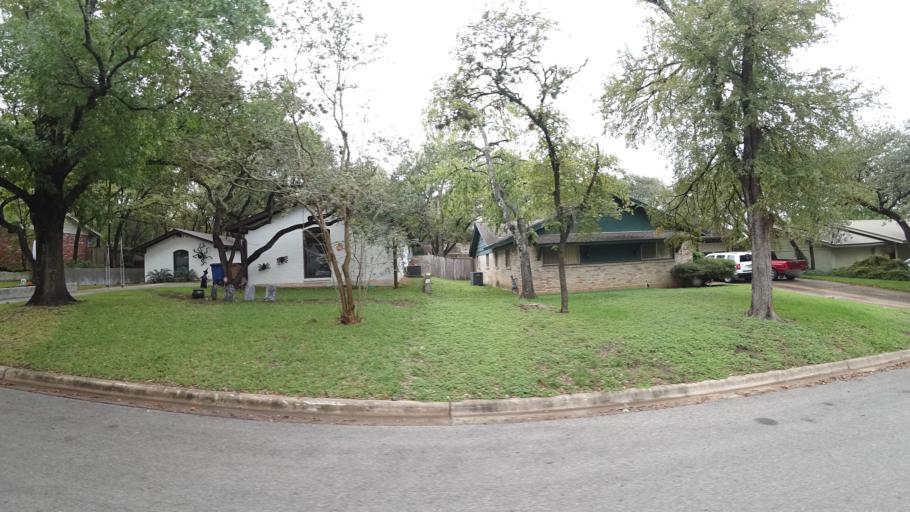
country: US
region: Texas
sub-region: Travis County
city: Rollingwood
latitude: 30.2589
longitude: -97.7779
